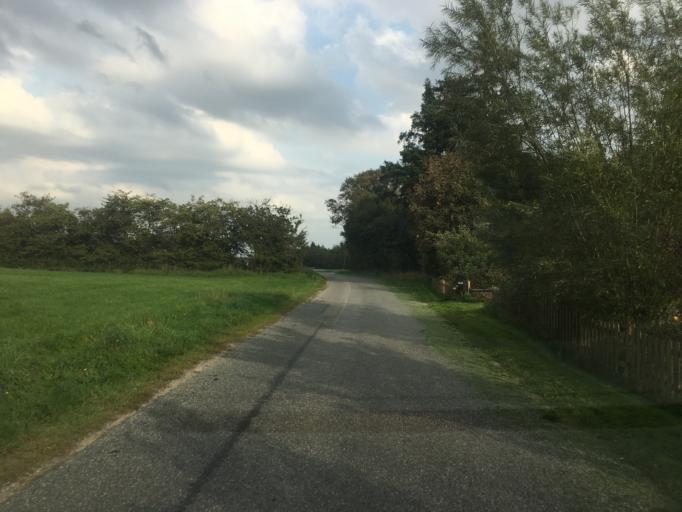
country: DK
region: South Denmark
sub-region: Tonder Kommune
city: Logumkloster
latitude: 55.0056
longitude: 9.0348
